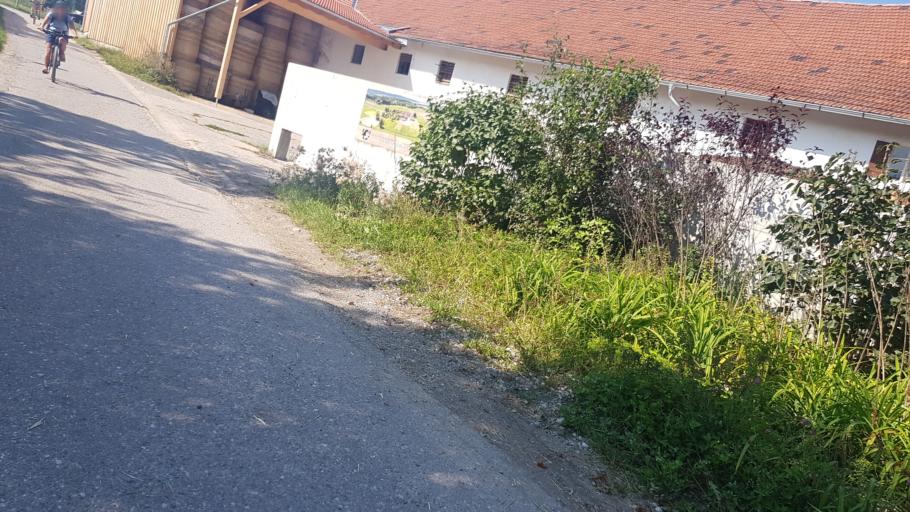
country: DE
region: Bavaria
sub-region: Upper Bavaria
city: Herrsching am Ammersee
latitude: 48.0243
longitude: 11.1602
